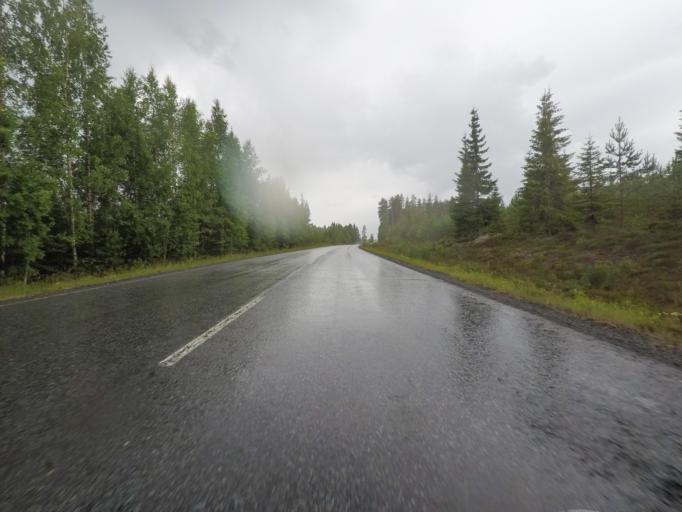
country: FI
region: Central Finland
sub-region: Jyvaeskylae
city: Toivakka
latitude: 62.1883
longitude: 26.1984
